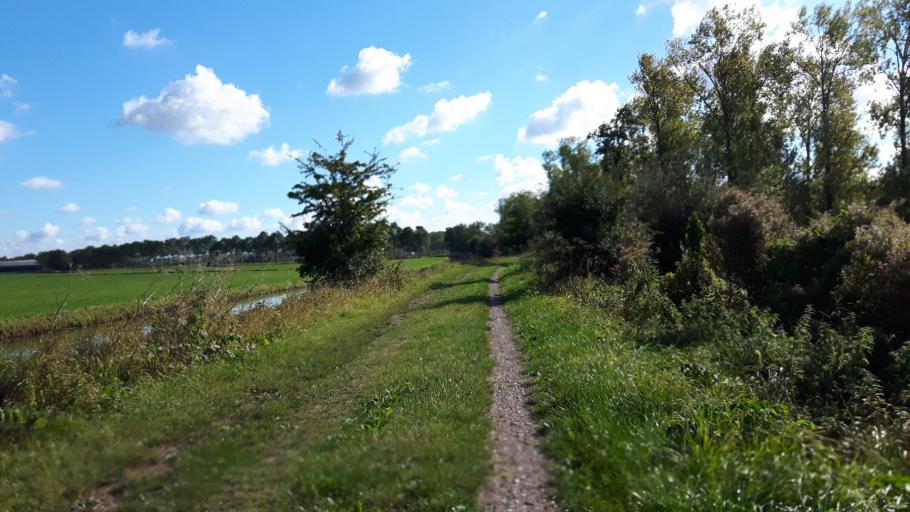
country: NL
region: Gelderland
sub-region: Gemeente Culemborg
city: Culemborg
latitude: 51.9346
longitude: 5.2587
